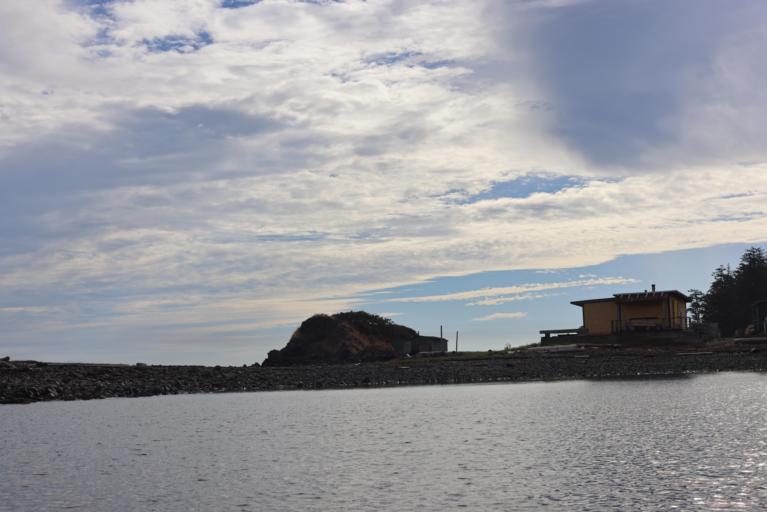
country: CA
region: British Columbia
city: Nanaimo
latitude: 49.2301
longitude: -123.9562
